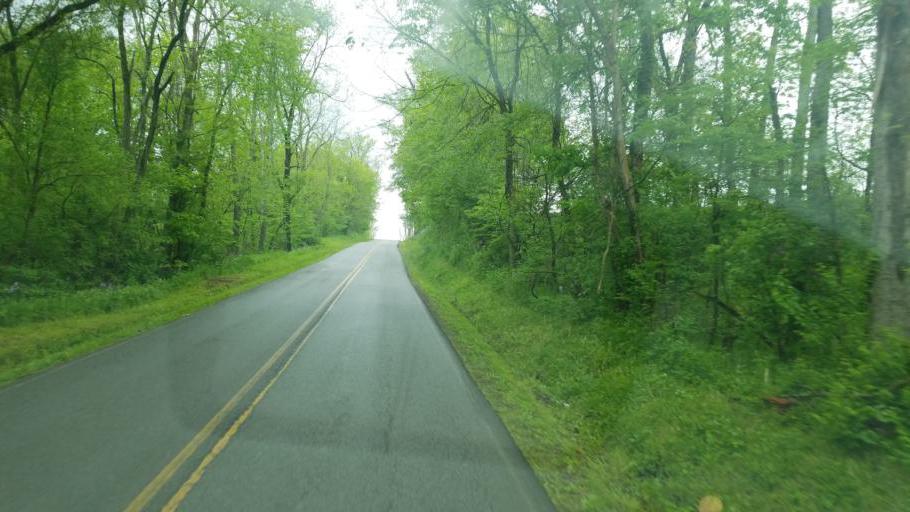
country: US
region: Ohio
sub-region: Harrison County
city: Cadiz
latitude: 40.2742
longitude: -80.9051
